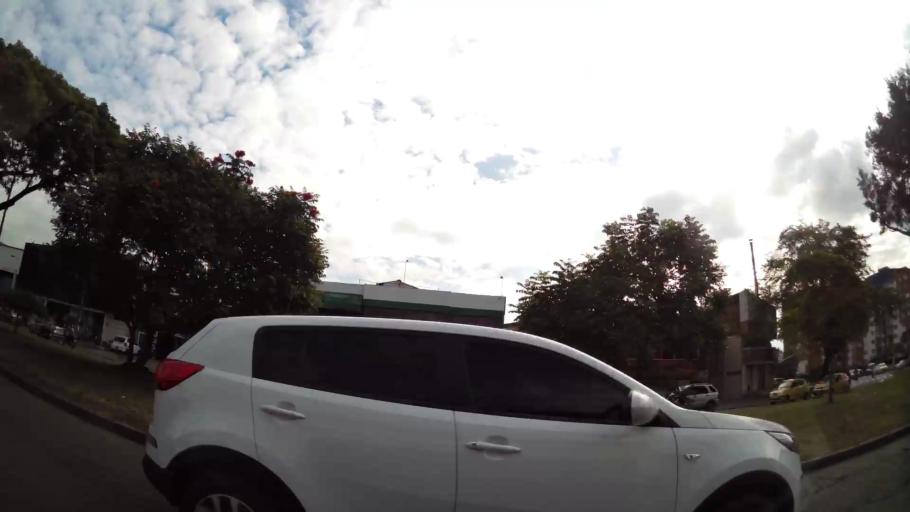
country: CO
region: Valle del Cauca
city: Cali
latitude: 3.4766
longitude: -76.5049
